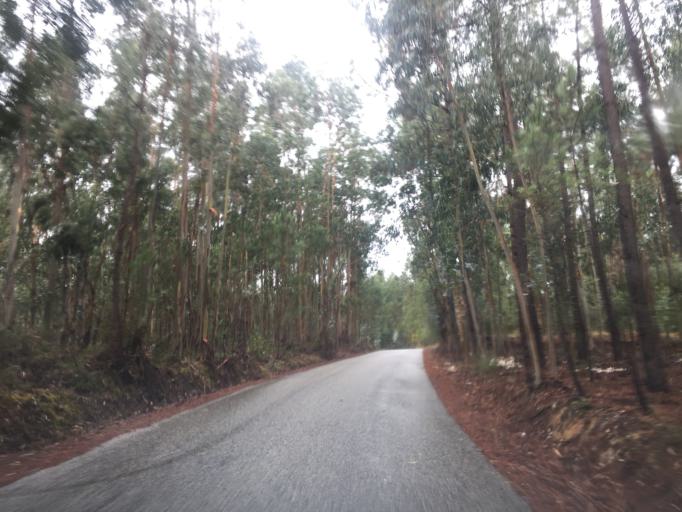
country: PT
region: Leiria
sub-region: Pombal
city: Lourical
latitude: 40.0510
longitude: -8.7794
